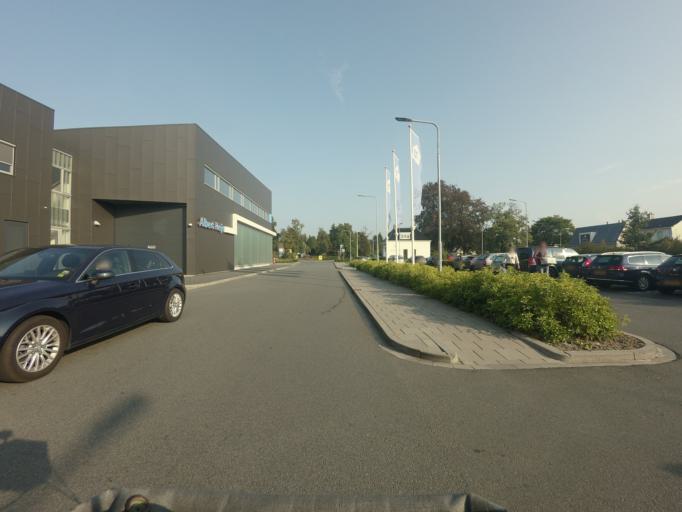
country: NL
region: Groningen
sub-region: Gemeente Haren
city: Haren
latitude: 53.1467
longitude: 6.5655
